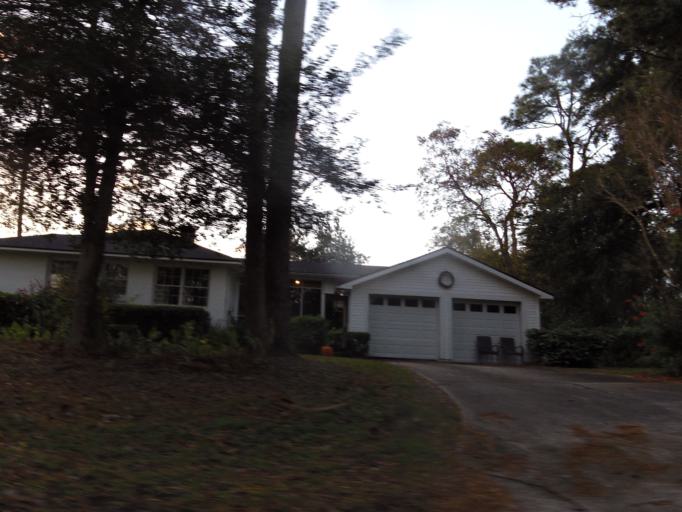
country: US
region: Florida
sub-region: Duval County
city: Jacksonville
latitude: 30.2815
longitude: -81.6553
